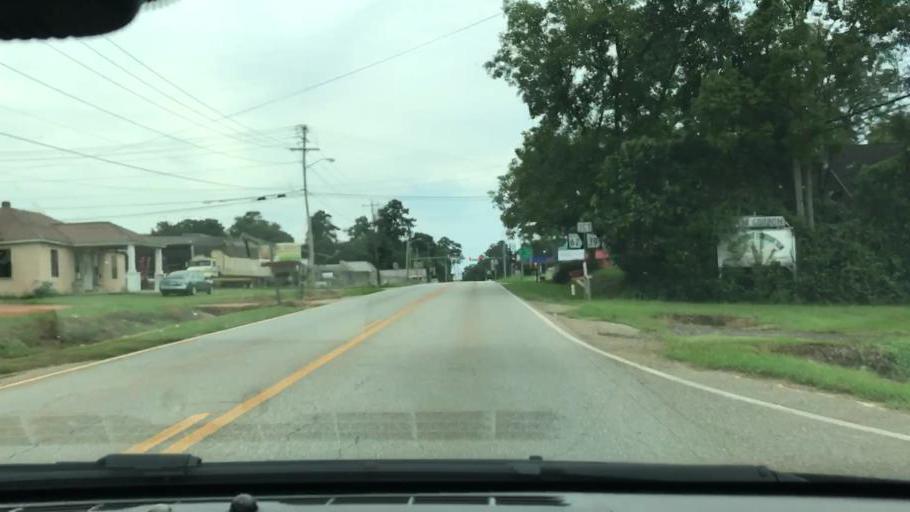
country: US
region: Georgia
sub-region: Early County
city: Blakely
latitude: 31.3935
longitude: -84.9331
